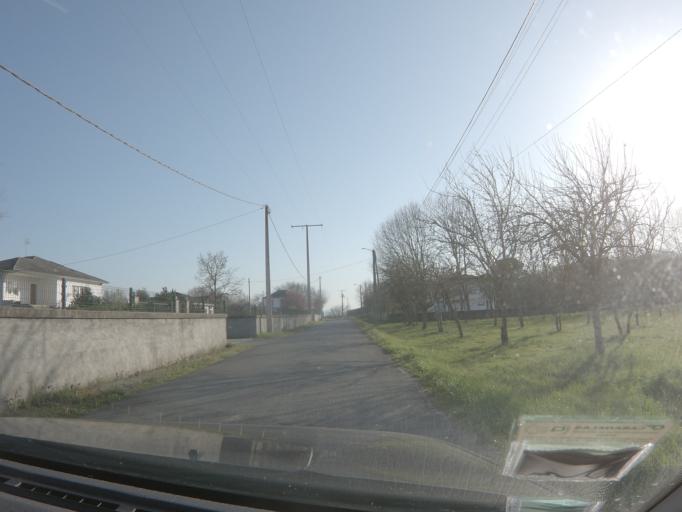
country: ES
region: Galicia
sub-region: Provincia de Lugo
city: Corgo
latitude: 42.9441
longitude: -7.4356
